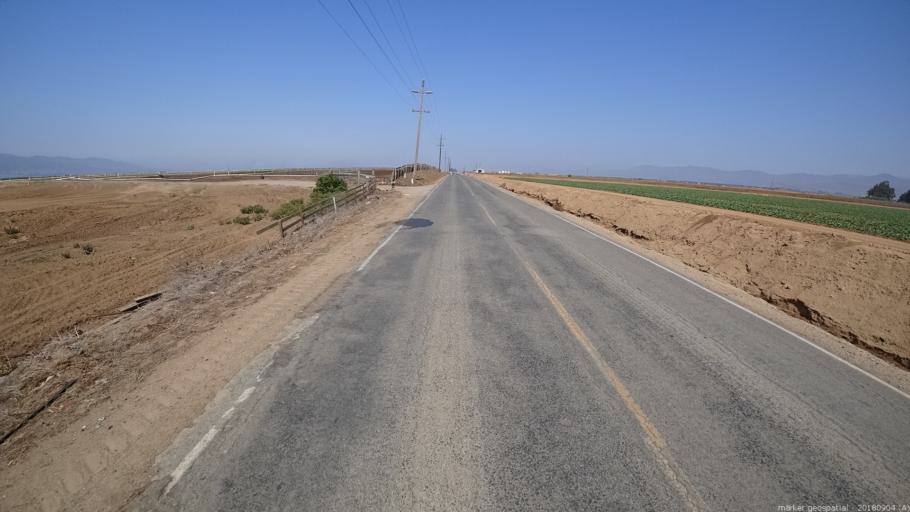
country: US
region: California
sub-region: Monterey County
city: Chualar
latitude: 36.5539
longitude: -121.4760
